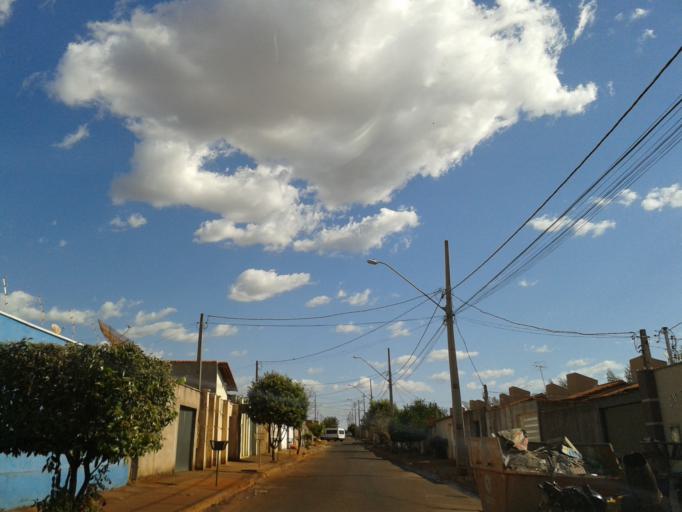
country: BR
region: Minas Gerais
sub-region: Capinopolis
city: Capinopolis
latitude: -18.6964
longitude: -49.5675
